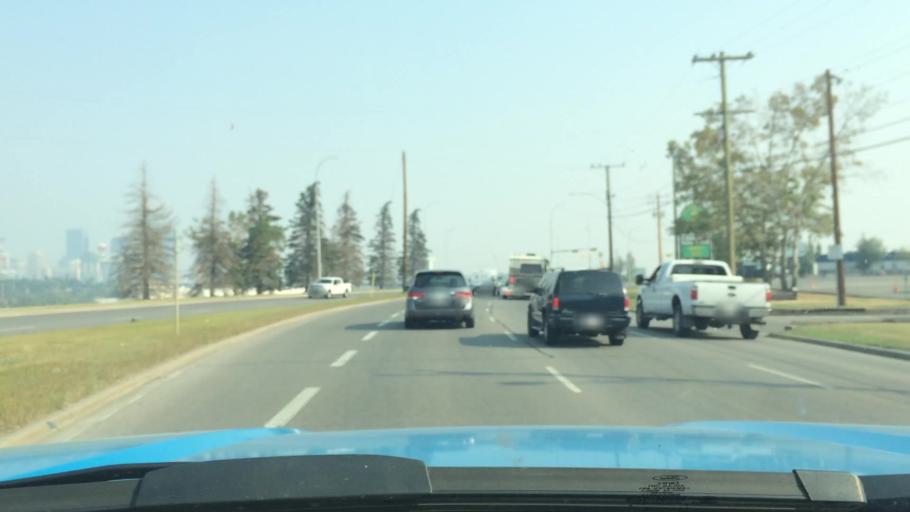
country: CA
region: Alberta
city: Calgary
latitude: 51.0193
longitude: -114.0484
